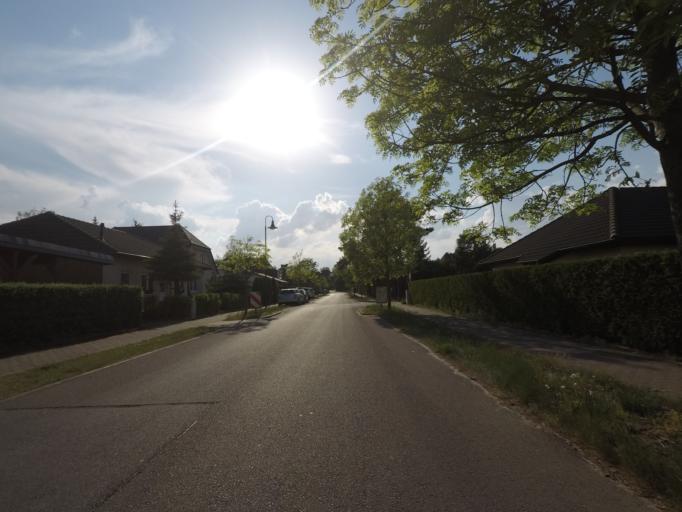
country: DE
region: Brandenburg
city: Melchow
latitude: 52.8356
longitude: 13.7246
